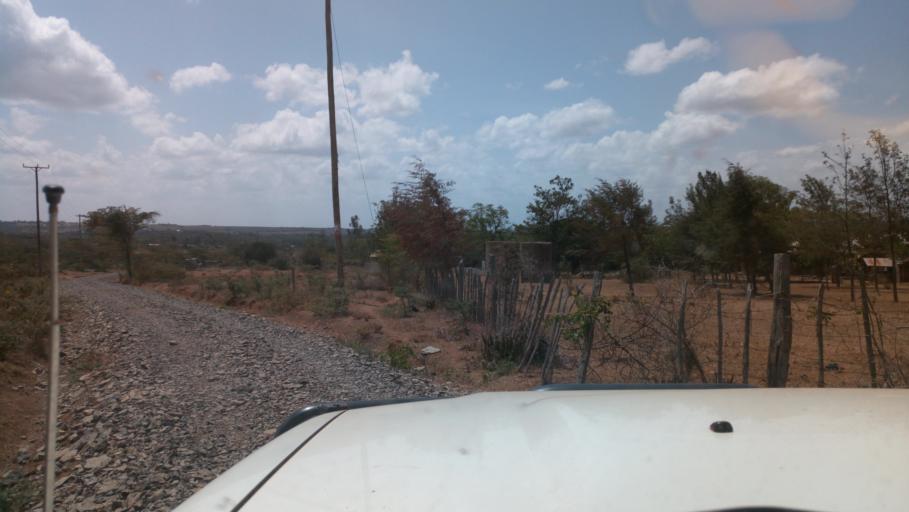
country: KE
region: Laikipia
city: Naro Moru
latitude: -0.1567
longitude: 36.8534
